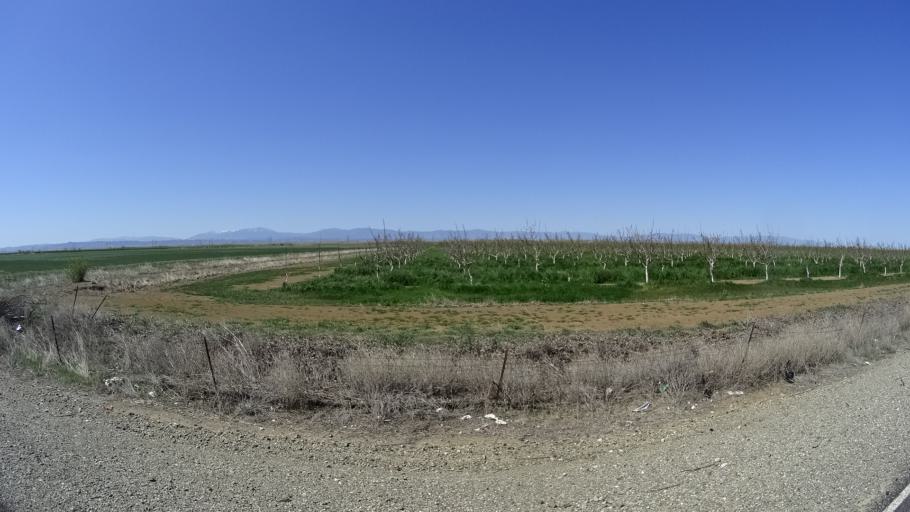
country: US
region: California
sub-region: Glenn County
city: Willows
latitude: 39.5827
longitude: -122.2497
